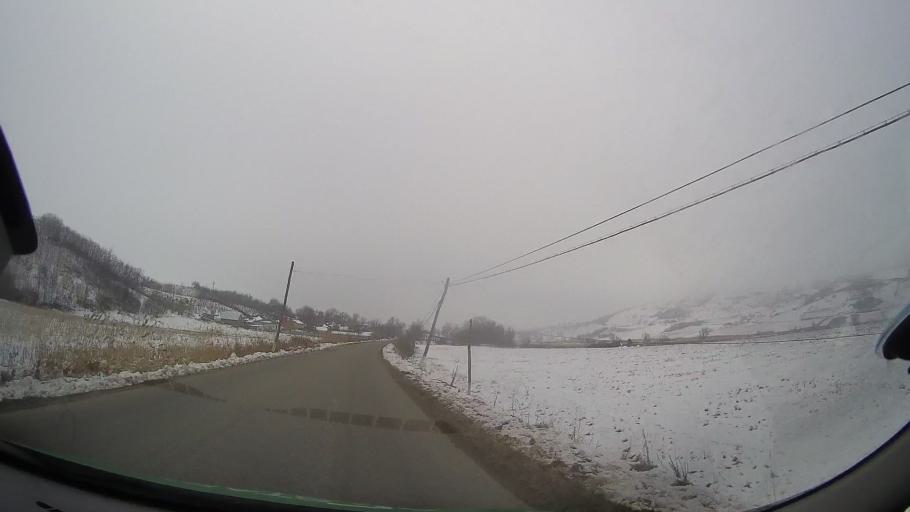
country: RO
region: Bacau
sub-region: Comuna Glavanesti
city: Frumuselu
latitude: 46.2918
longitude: 27.3010
